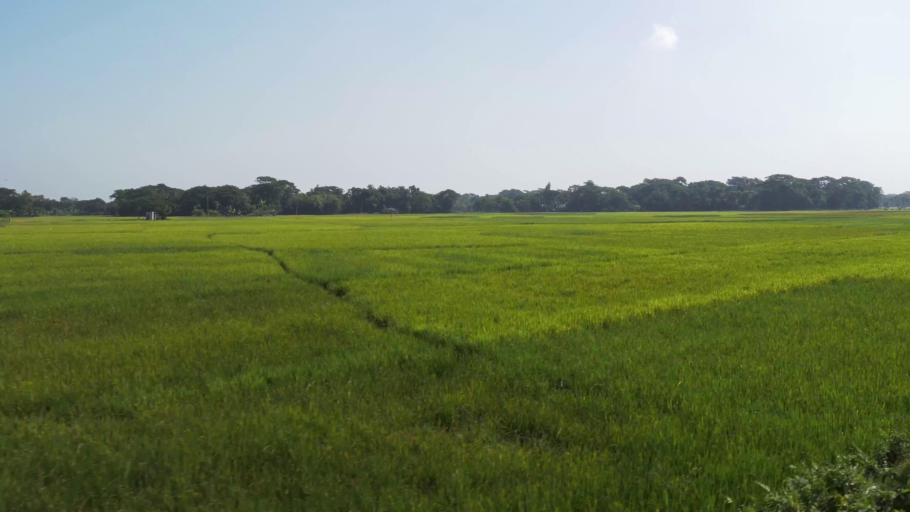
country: BD
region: Dhaka
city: Gafargaon
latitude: 24.5178
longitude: 90.5104
